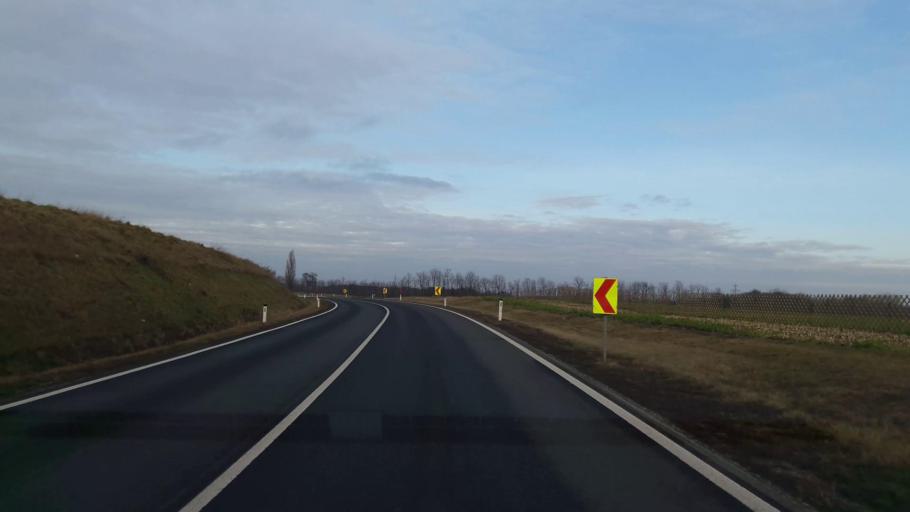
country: AT
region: Lower Austria
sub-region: Politischer Bezirk Mistelbach
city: Staatz
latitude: 48.6864
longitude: 16.4727
